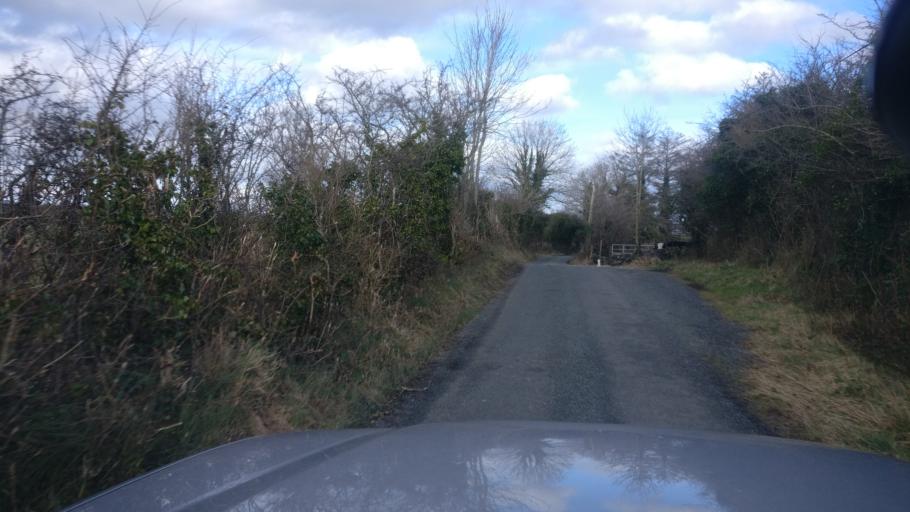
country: IE
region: Connaught
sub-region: County Galway
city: Loughrea
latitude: 53.2044
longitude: -8.4295
